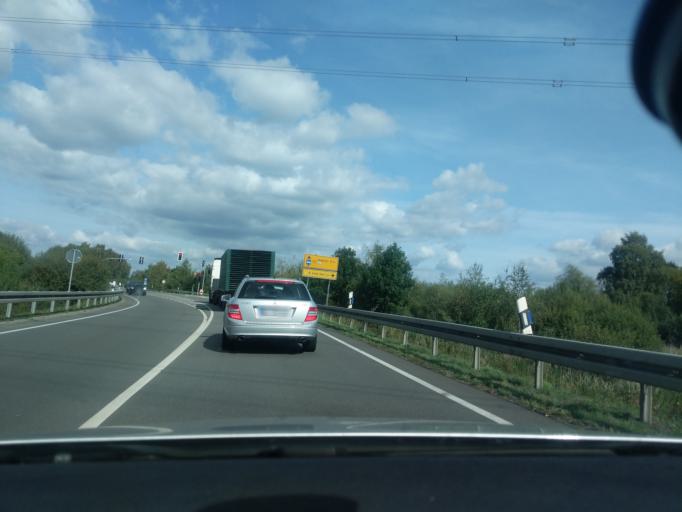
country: DE
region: Lower Saxony
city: Bohmte
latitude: 52.3568
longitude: 8.2976
